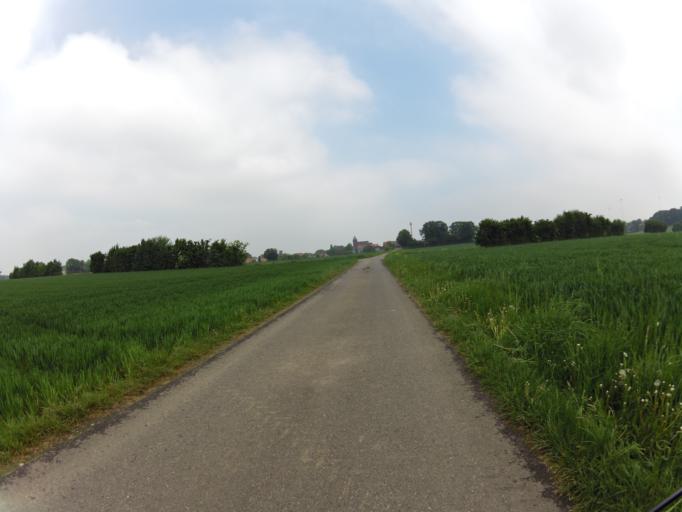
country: DE
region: North Rhine-Westphalia
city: Geilenkirchen
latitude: 51.0167
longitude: 6.1320
